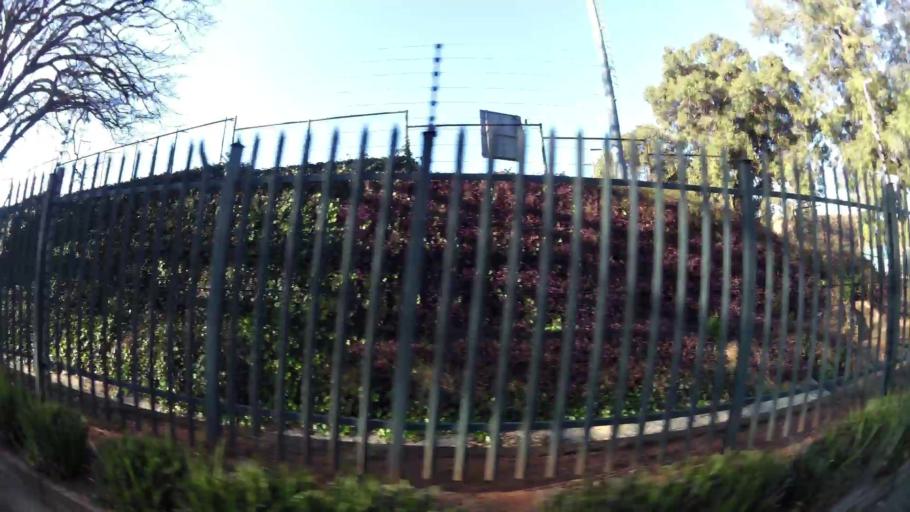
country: ZA
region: Gauteng
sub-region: City of Johannesburg Metropolitan Municipality
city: Johannesburg
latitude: -26.1755
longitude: 28.0546
